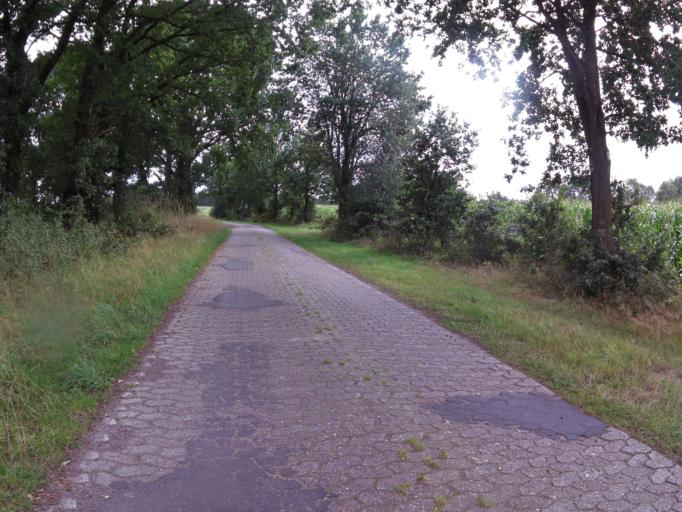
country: DE
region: Lower Saxony
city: Hipstedt
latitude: 53.5019
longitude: 8.9184
